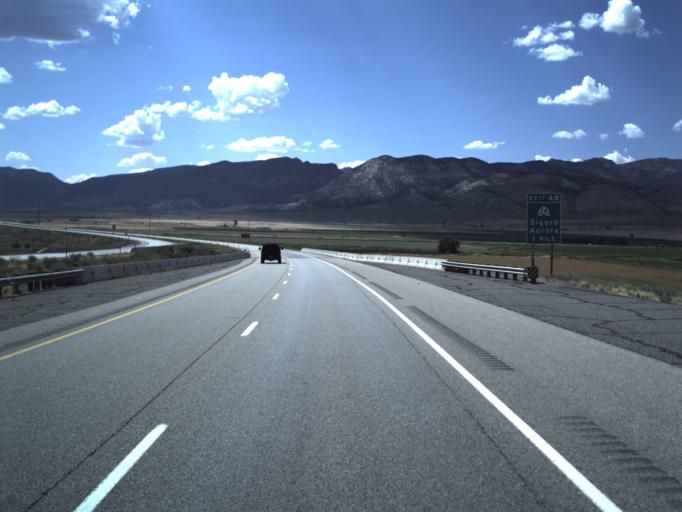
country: US
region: Utah
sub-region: Sevier County
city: Aurora
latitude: 38.8798
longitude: -111.9424
